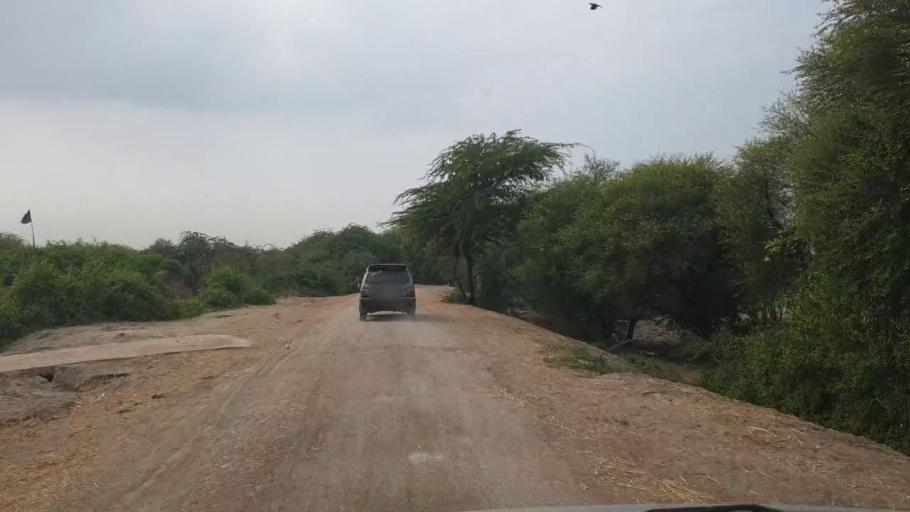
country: PK
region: Sindh
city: Talhar
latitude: 24.9209
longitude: 68.7800
